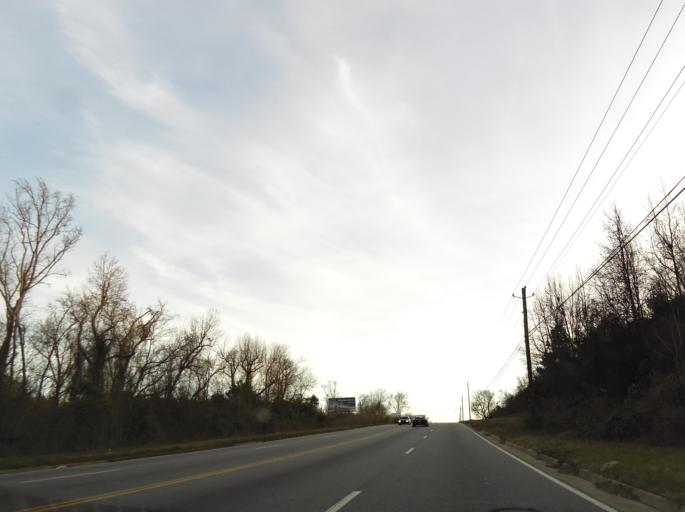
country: US
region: Georgia
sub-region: Bibb County
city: Macon
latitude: 32.8027
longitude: -83.6406
